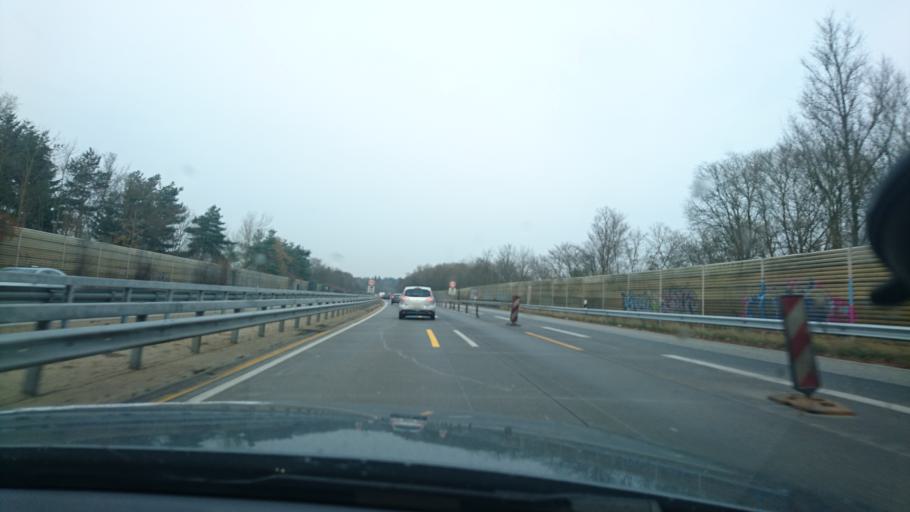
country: DE
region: Schleswig-Holstein
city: Bad Schwartau
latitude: 53.9217
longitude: 10.7253
